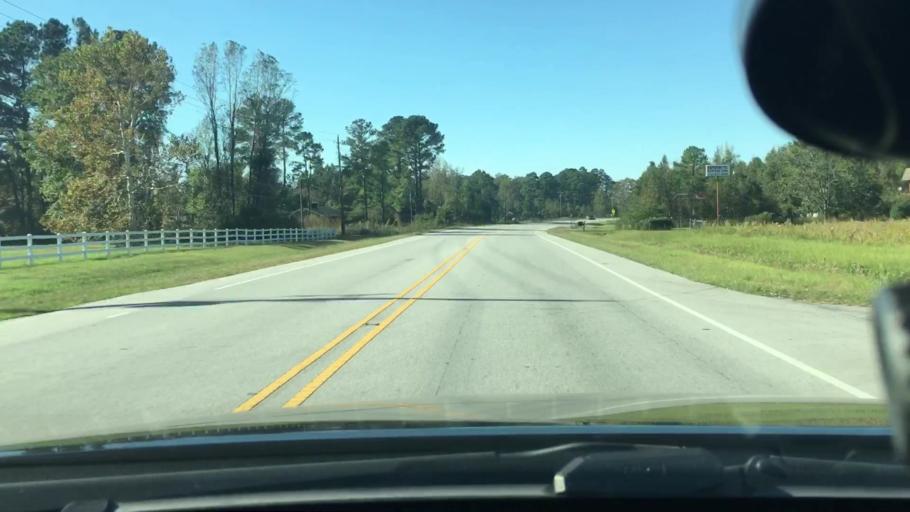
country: US
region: North Carolina
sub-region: Craven County
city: Trent Woods
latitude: 35.1593
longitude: -77.1163
